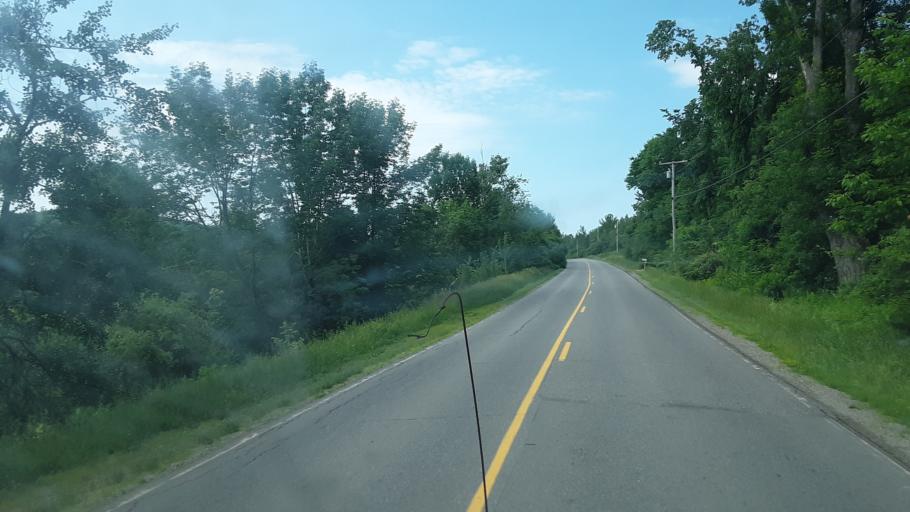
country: US
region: Maine
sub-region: Waldo County
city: Frankfort
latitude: 44.6045
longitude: -68.9370
